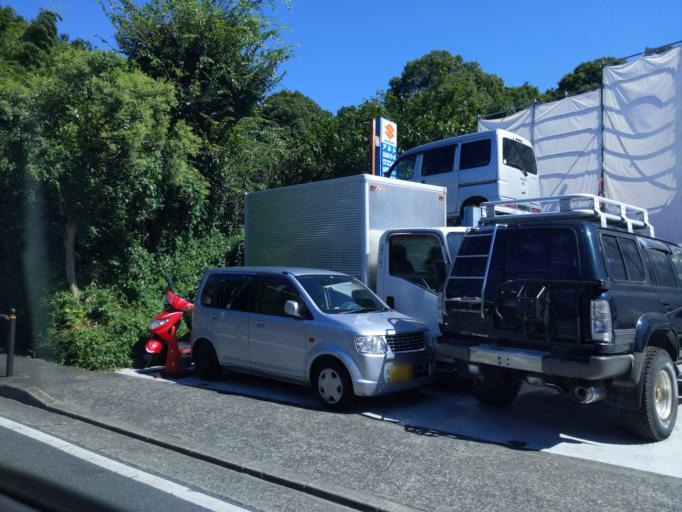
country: JP
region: Tokyo
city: Chofugaoka
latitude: 35.6518
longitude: 139.5850
